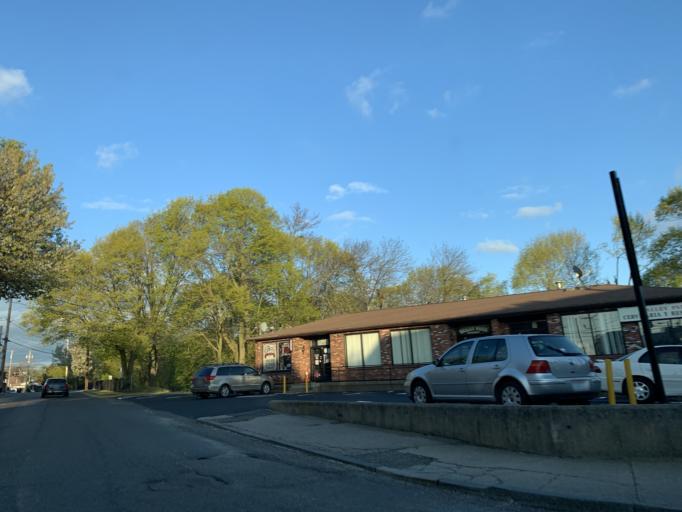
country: US
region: Rhode Island
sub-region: Providence County
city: Valley Falls
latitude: 41.9002
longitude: -71.3907
